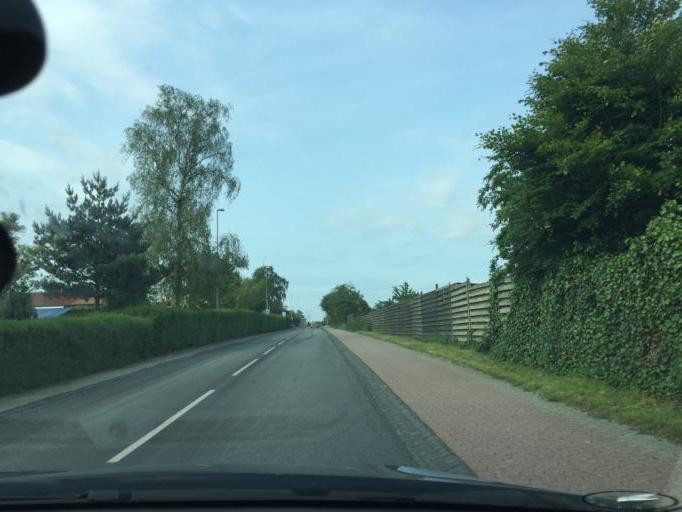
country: DK
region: South Denmark
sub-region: Odense Kommune
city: Bellinge
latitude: 55.3343
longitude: 10.3236
